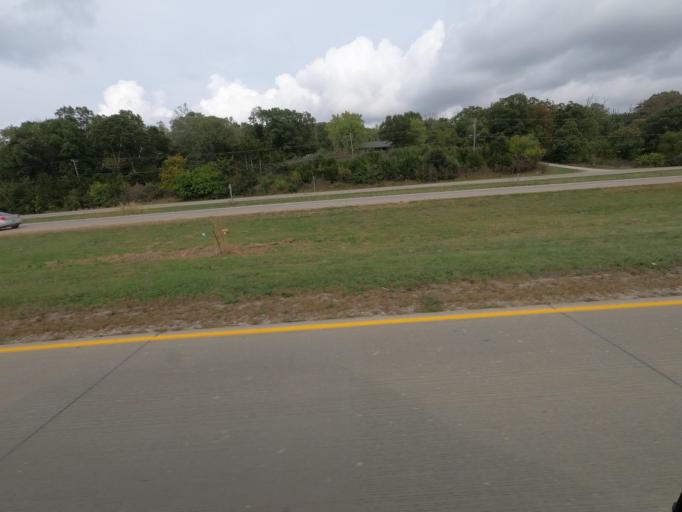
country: US
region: Iowa
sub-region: Wapello County
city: Ottumwa
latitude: 41.0012
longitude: -92.3503
